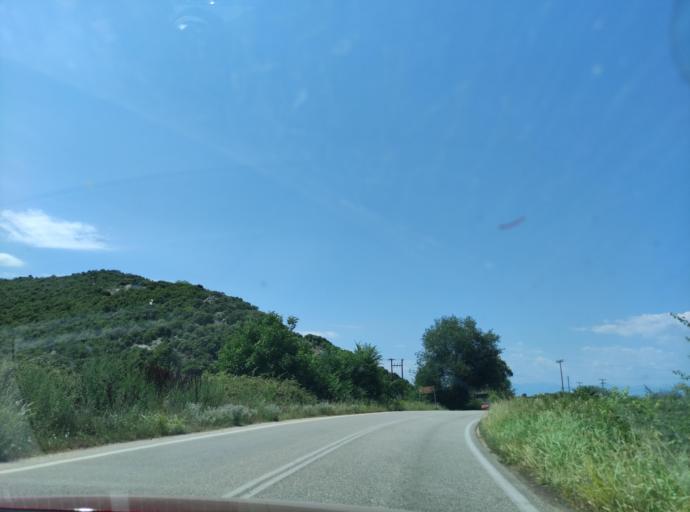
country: GR
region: East Macedonia and Thrace
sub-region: Nomos Kavalas
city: Palaiochori
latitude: 40.9649
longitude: 24.1816
